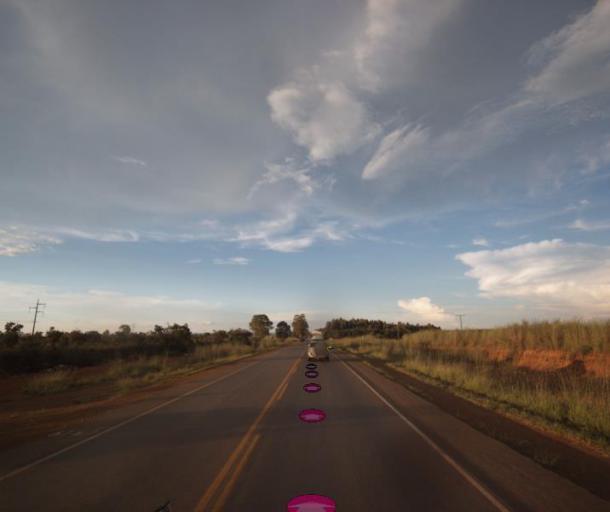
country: BR
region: Goias
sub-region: Anapolis
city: Anapolis
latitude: -16.2240
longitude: -48.9245
